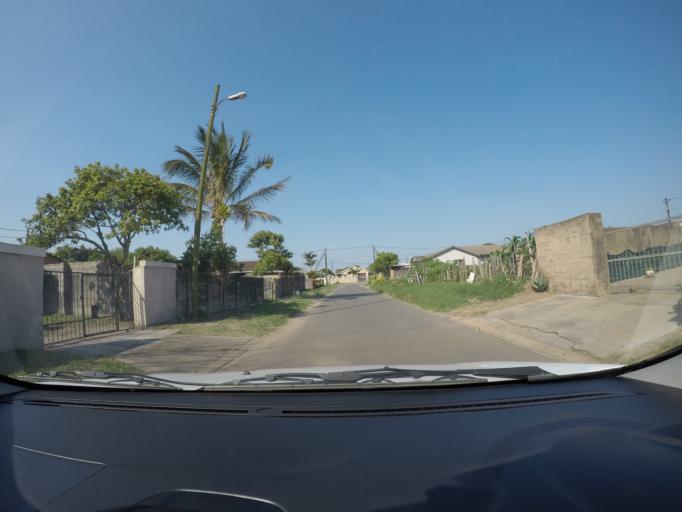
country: ZA
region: KwaZulu-Natal
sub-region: uThungulu District Municipality
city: Richards Bay
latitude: -28.7207
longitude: 32.0371
